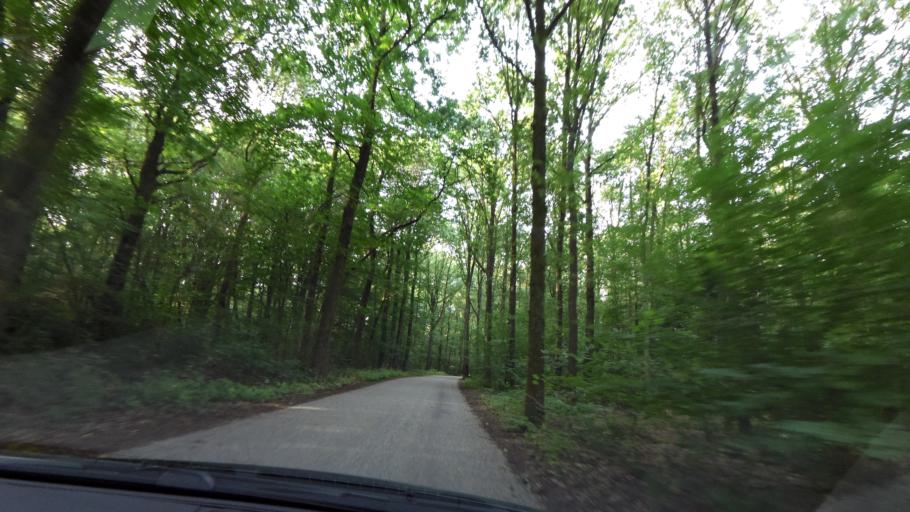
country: BE
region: Wallonia
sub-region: Province de Liege
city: Plombieres
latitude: 50.7676
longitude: 5.9618
